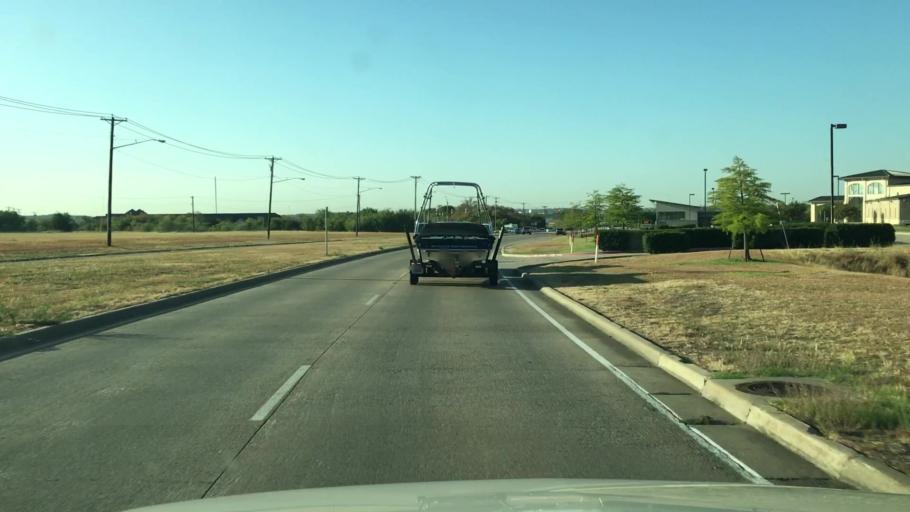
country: US
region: Texas
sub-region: Johnson County
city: Burleson
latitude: 32.5321
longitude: -97.3536
